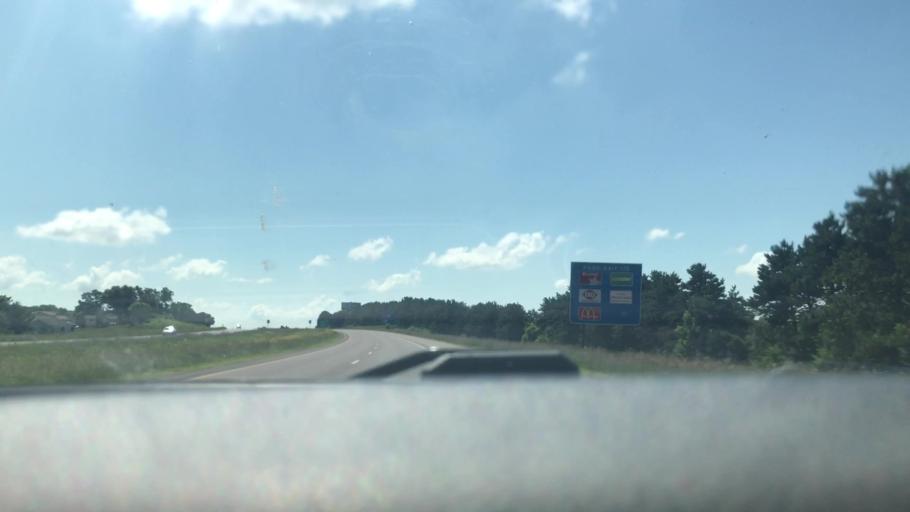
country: US
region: Wisconsin
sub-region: Chippewa County
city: Bloomer
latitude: 45.1070
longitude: -91.5146
